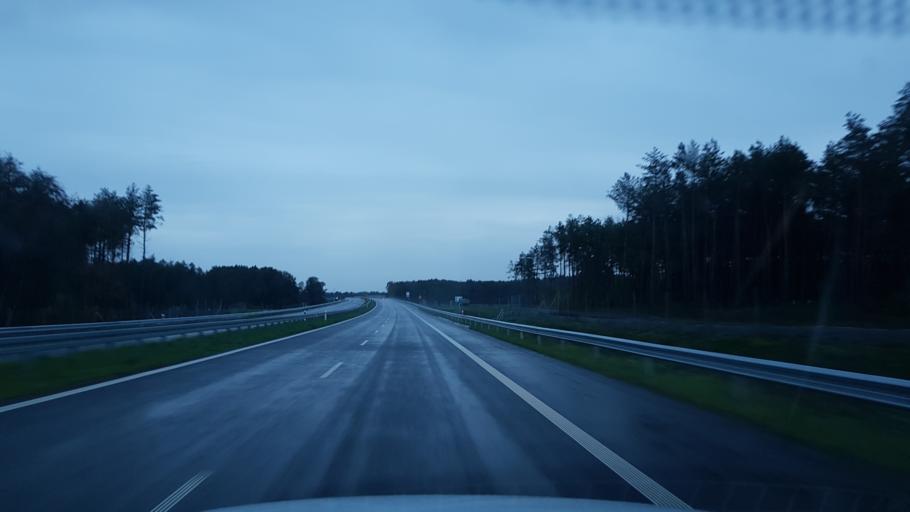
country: PL
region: West Pomeranian Voivodeship
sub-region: Powiat gryficki
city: Brojce
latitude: 53.9535
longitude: 15.4124
